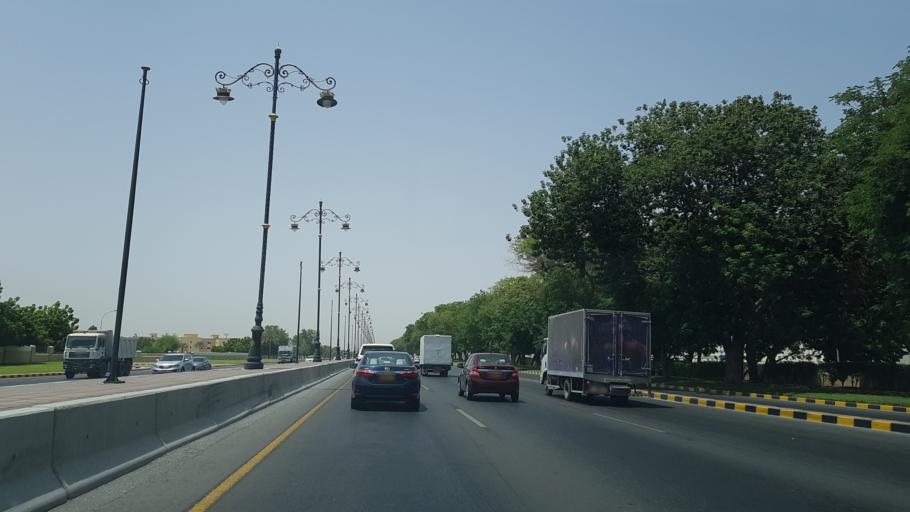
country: OM
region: Muhafazat Masqat
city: Bawshar
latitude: 23.5853
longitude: 58.2857
